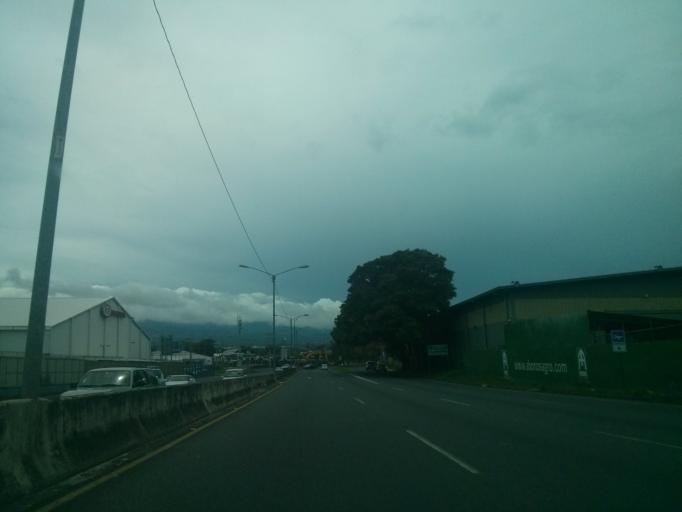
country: CR
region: San Jose
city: Colima
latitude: 9.9489
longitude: -84.1038
